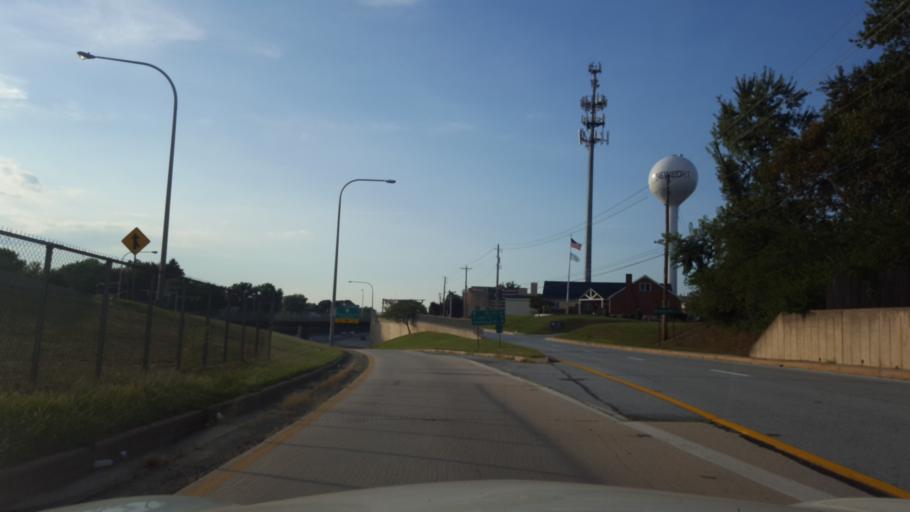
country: US
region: Delaware
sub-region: New Castle County
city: Newport
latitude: 39.7161
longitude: -75.6093
